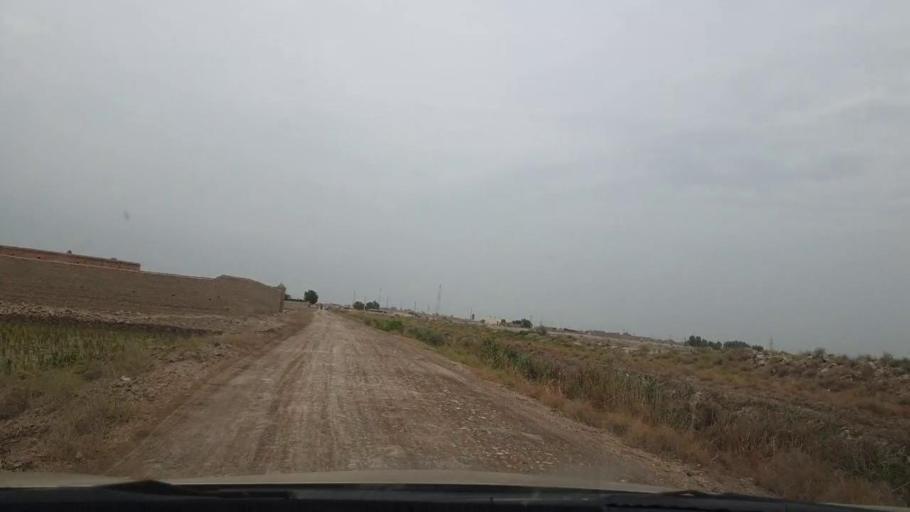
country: PK
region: Sindh
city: Ratodero
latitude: 27.7815
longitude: 68.2814
